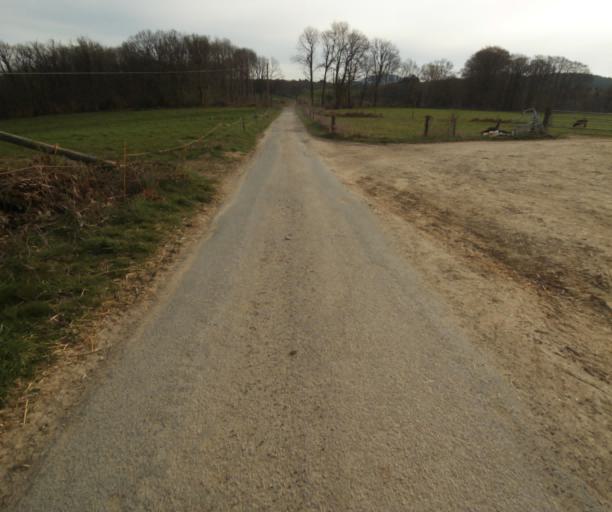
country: FR
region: Limousin
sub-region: Departement de la Correze
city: Chamboulive
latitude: 45.4607
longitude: 1.7592
